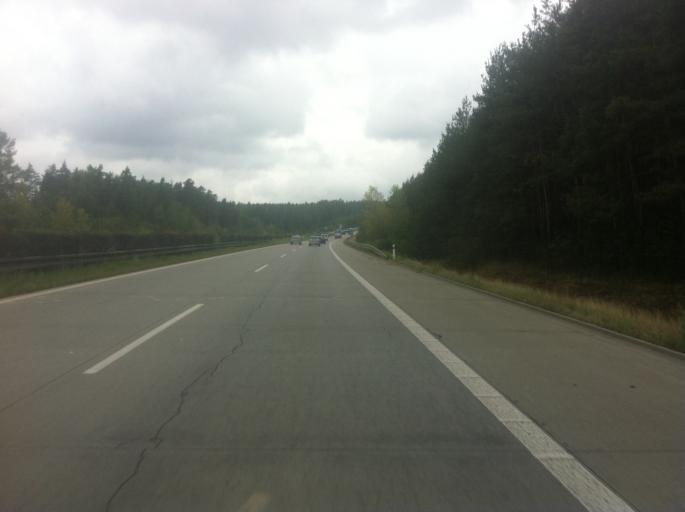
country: CZ
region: Plzensky
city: Hermanova Hut'
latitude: 49.7130
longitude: 13.0629
